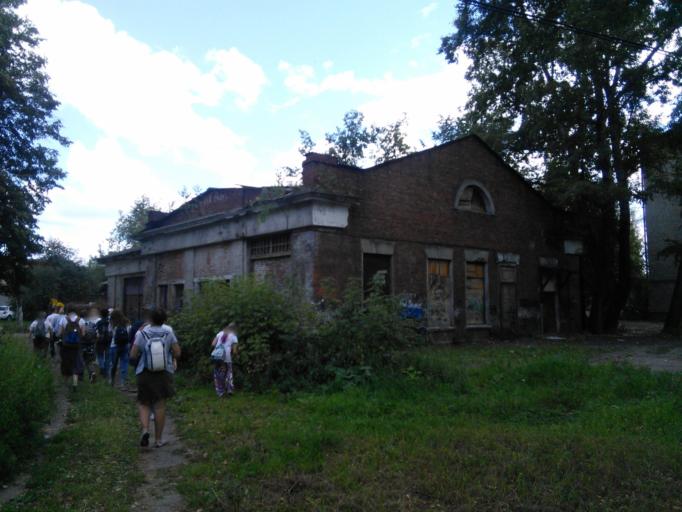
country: RU
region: Moskovskaya
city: Pavlovskiy Posad
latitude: 55.7704
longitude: 38.6516
